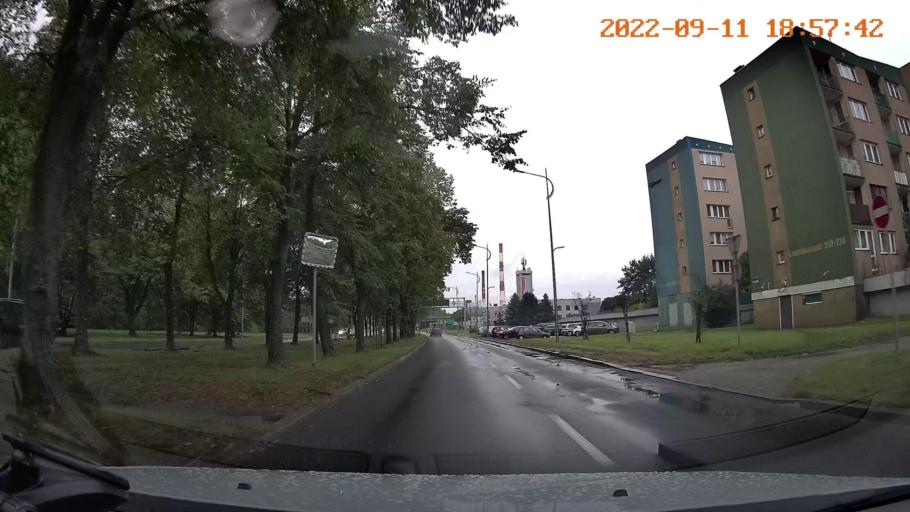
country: PL
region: Silesian Voivodeship
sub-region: Tychy
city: Cielmice
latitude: 50.1105
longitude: 19.0046
